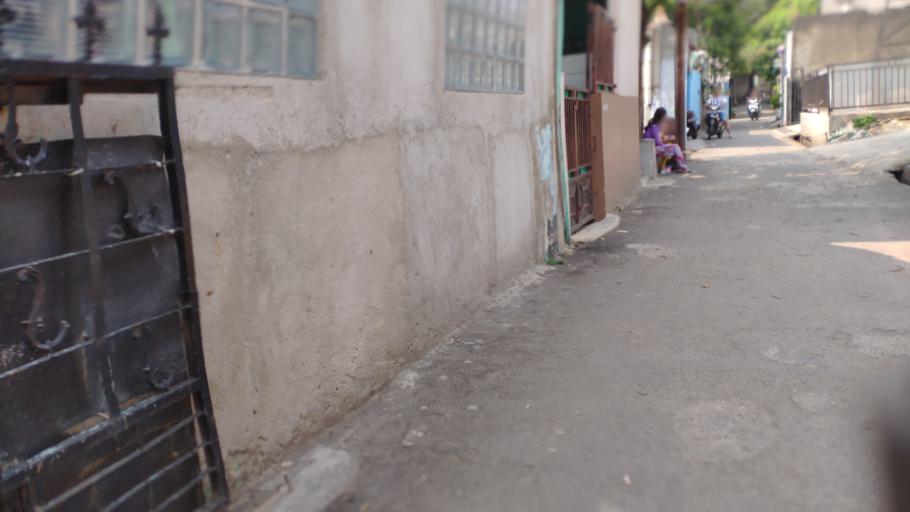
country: ID
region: West Java
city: Pamulang
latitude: -6.3132
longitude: 106.8103
